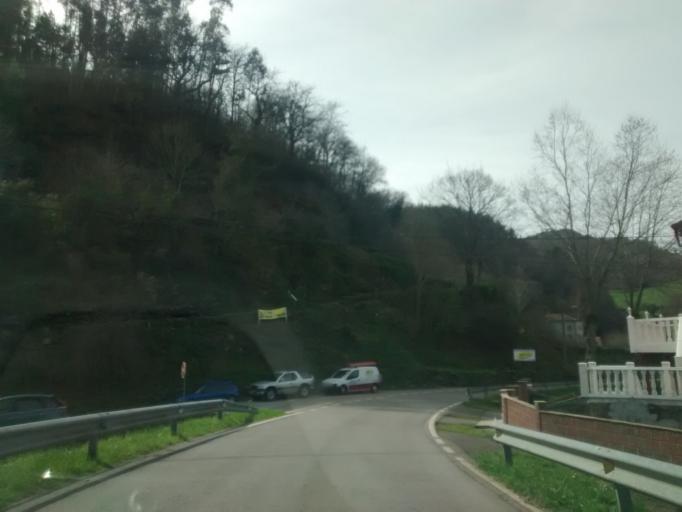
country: ES
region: Cantabria
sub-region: Provincia de Cantabria
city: Santiurde de Toranzo
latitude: 43.1683
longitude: -3.8947
